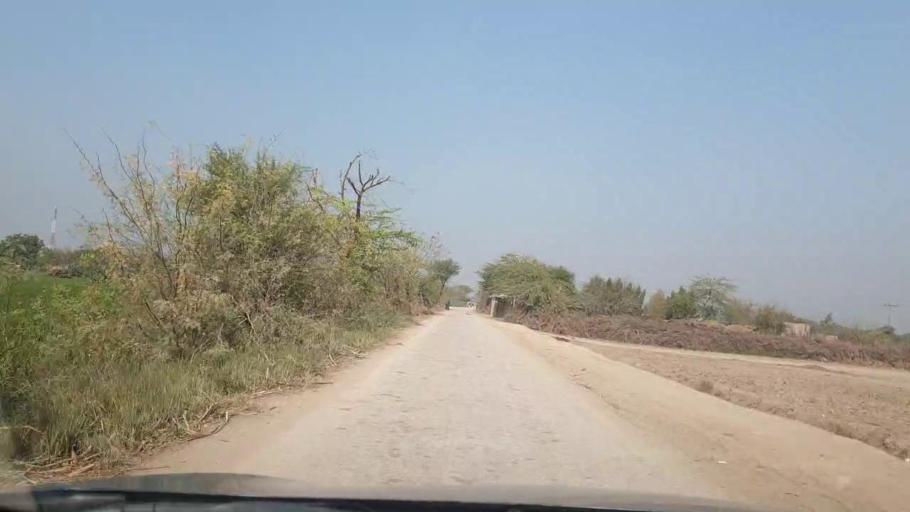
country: PK
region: Sindh
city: Tando Allahyar
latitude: 25.4991
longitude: 68.7960
